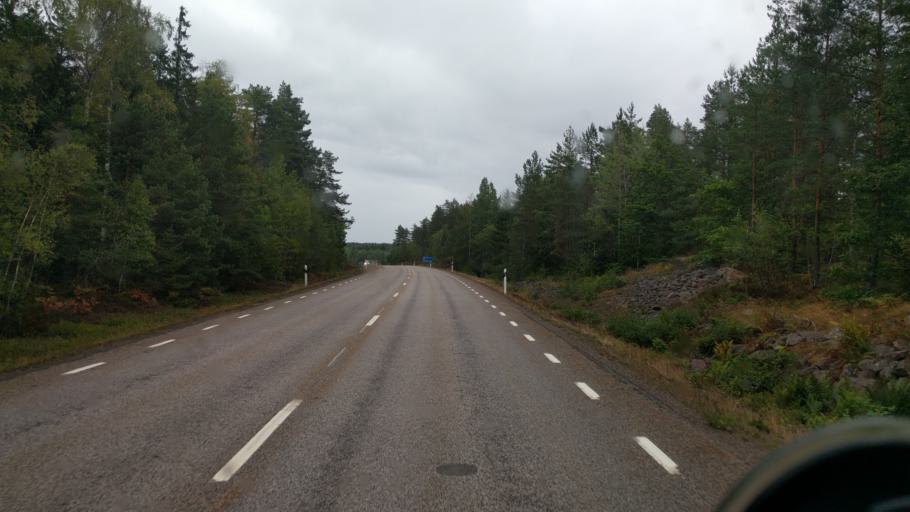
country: SE
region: Kalmar
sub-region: Vasterviks Kommun
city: Ankarsrum
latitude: 57.7047
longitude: 16.3238
